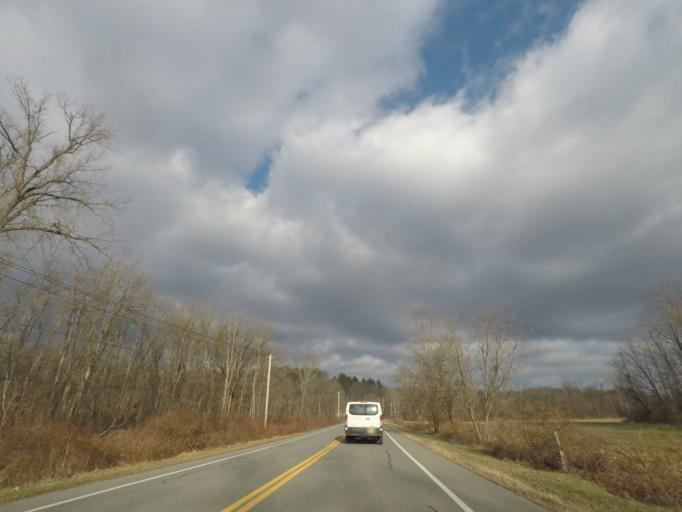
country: US
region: New York
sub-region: Albany County
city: Westmere
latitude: 42.6680
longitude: -73.8954
